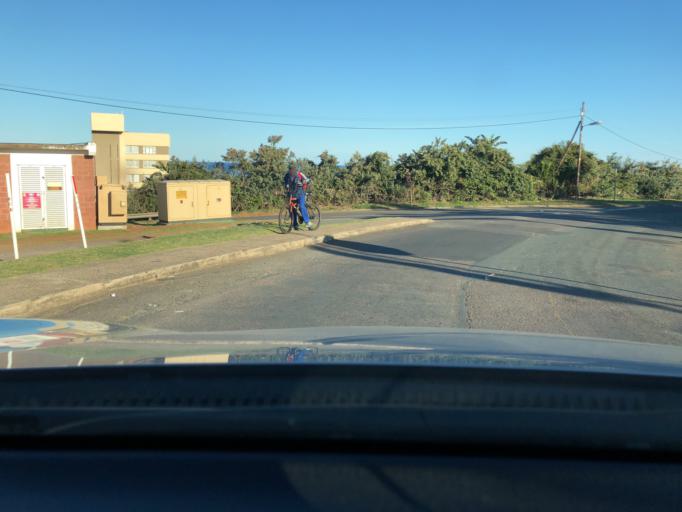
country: ZA
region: KwaZulu-Natal
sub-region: eThekwini Metropolitan Municipality
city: Umkomaas
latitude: -30.0453
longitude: 30.8911
